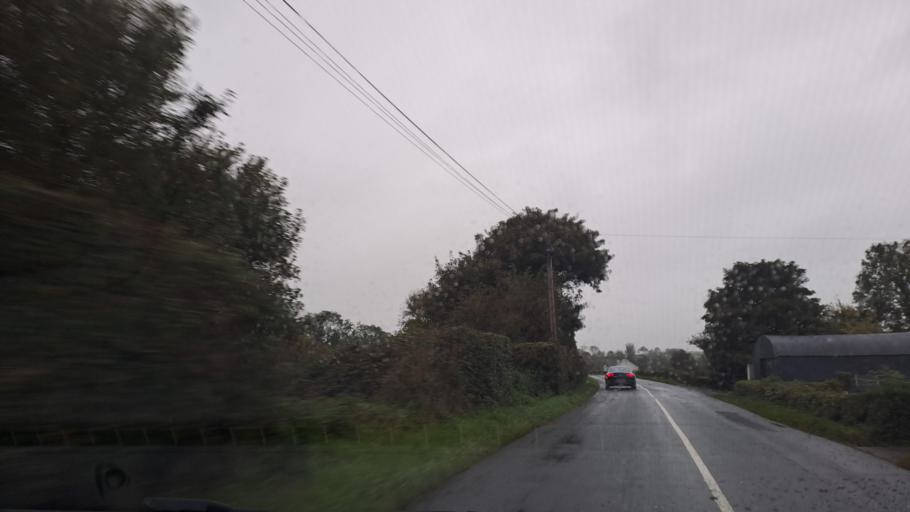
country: IE
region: Ulster
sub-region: County Monaghan
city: Monaghan
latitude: 54.2164
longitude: -6.9105
